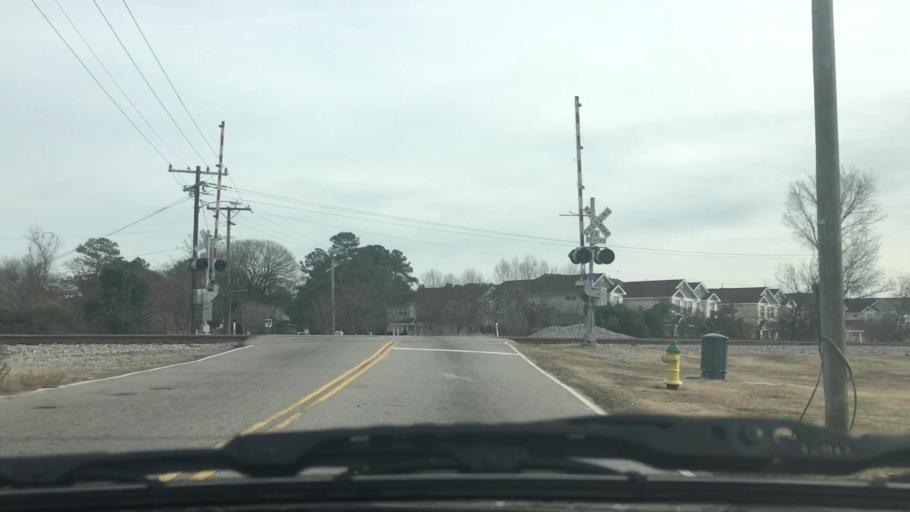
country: US
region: Virginia
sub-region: City of Norfolk
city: Norfolk
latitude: 36.8905
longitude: -76.2550
